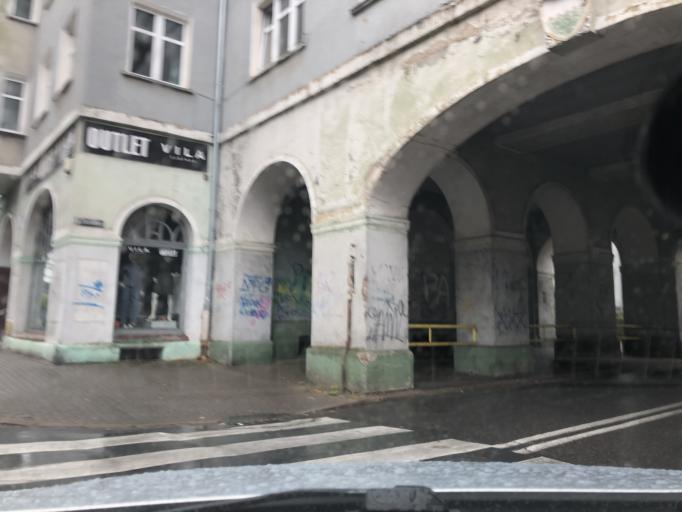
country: PL
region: Greater Poland Voivodeship
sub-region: Powiat pilski
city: Pila
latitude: 53.1473
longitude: 16.7330
